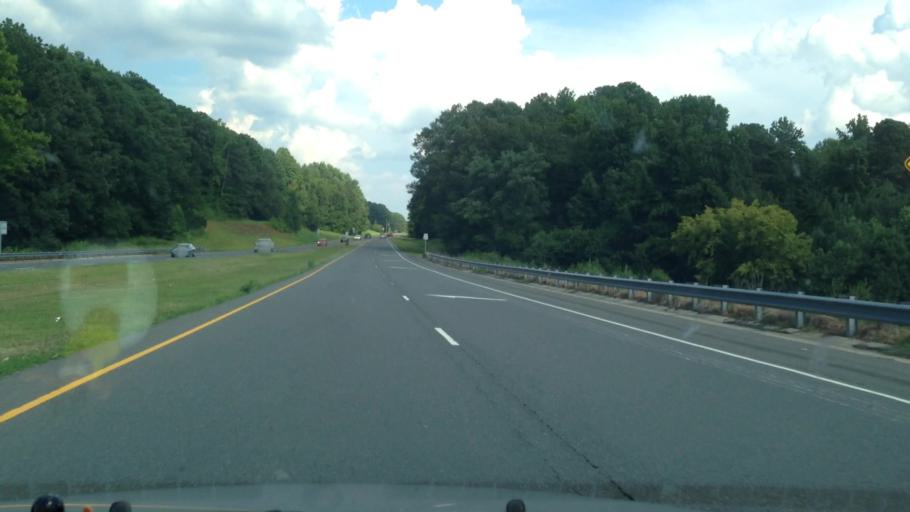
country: US
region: North Carolina
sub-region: Lee County
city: Broadway
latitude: 35.4465
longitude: -79.1173
